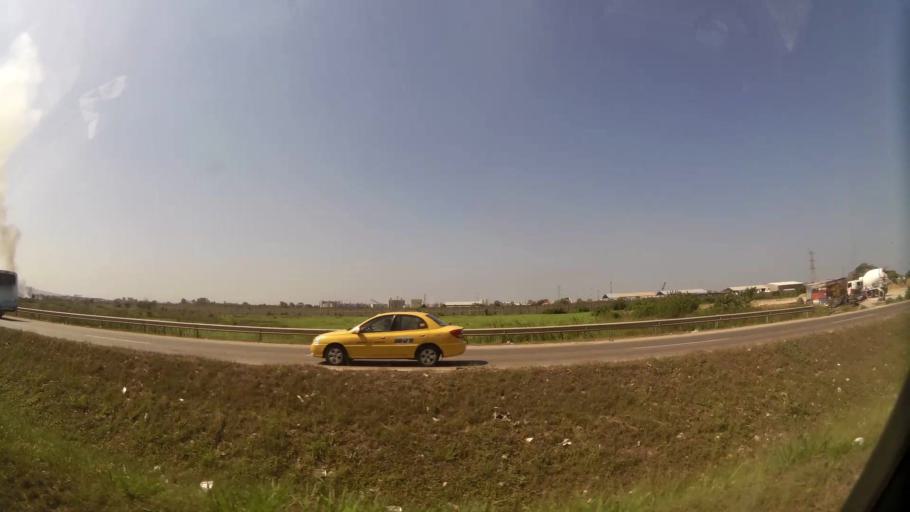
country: CO
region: Bolivar
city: Cartagena
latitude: 10.4055
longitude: -75.4483
